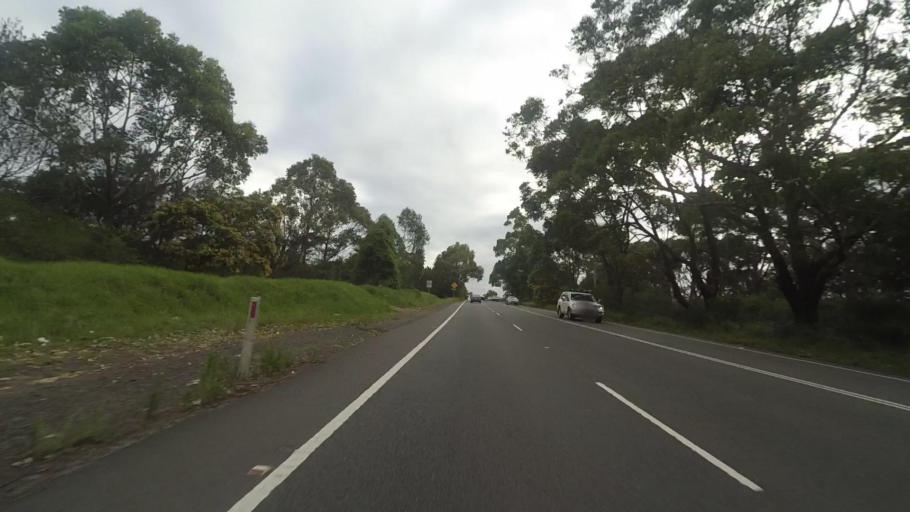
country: AU
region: New South Wales
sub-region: Sutherland Shire
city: Menai
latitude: -34.0380
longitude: 151.0000
